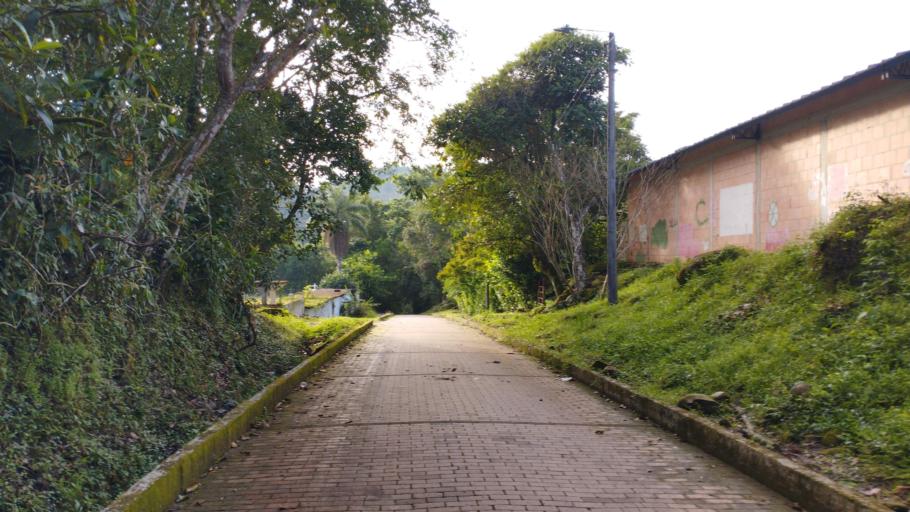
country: CO
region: Boyaca
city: San Luis de Gaceno
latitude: 4.8200
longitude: -73.1662
